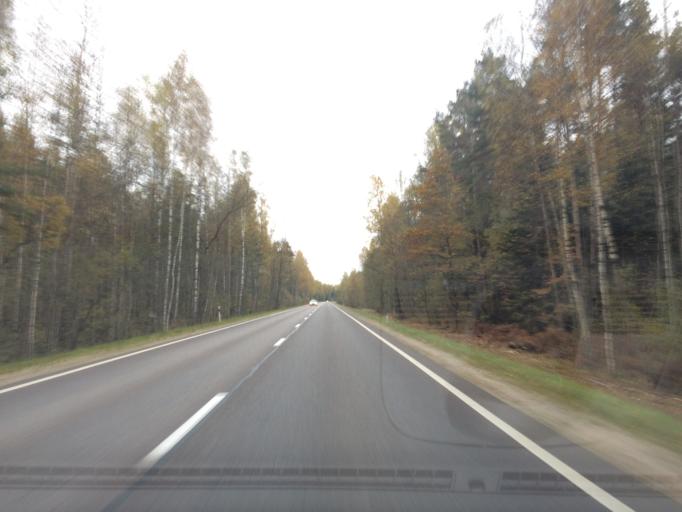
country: LV
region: Livani
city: Livani
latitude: 56.5395
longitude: 26.1297
